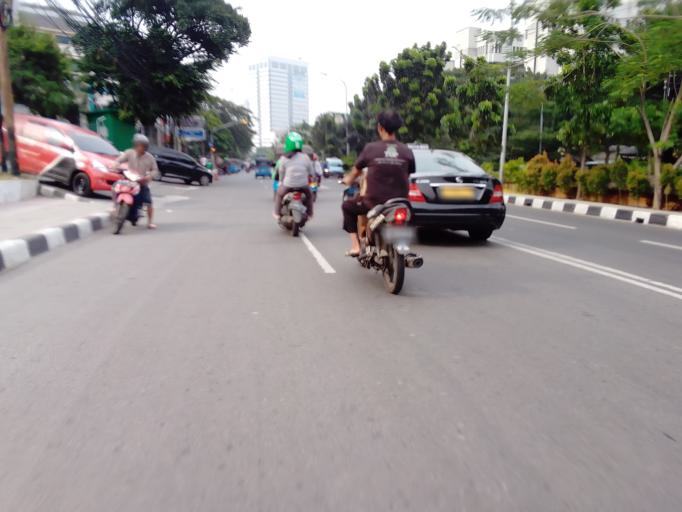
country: ID
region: Jakarta Raya
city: Jakarta
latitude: -6.1786
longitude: 106.8187
